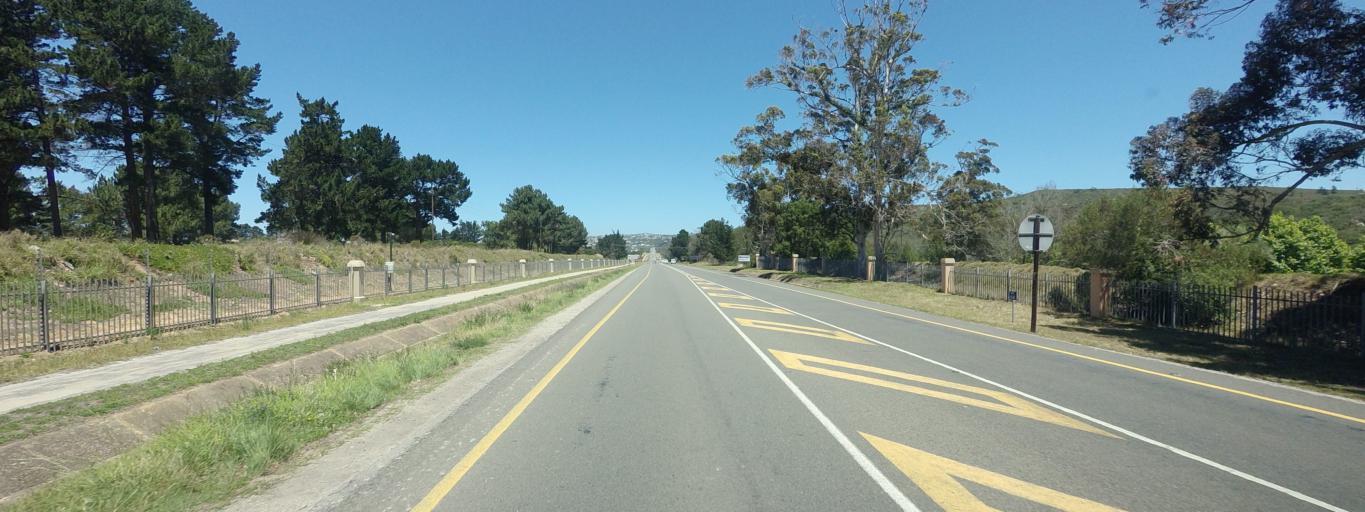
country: ZA
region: Western Cape
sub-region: Eden District Municipality
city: Plettenberg Bay
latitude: -34.0231
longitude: 23.3812
